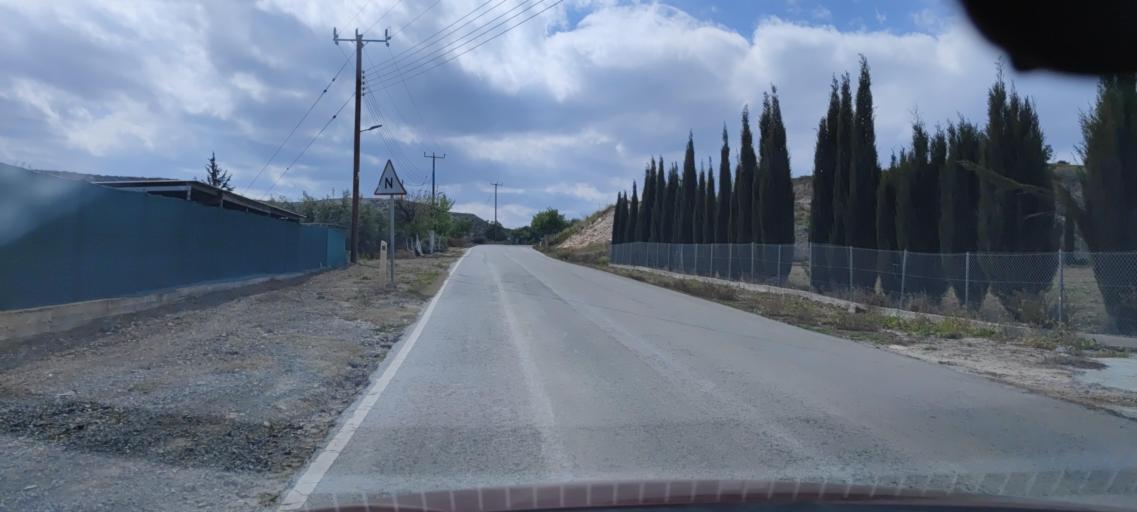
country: CY
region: Lefkosia
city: Pera
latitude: 35.0202
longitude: 33.3016
